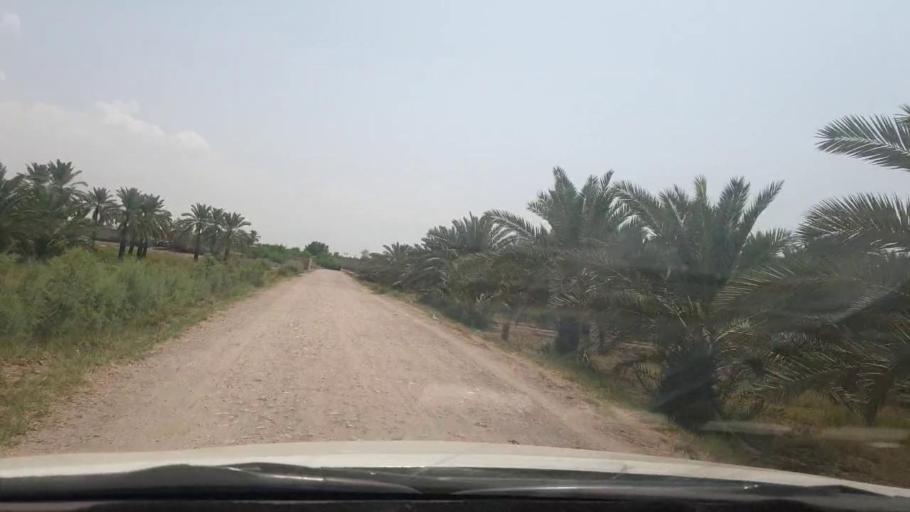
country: PK
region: Sindh
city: Khairpur
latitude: 27.5604
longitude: 68.8294
